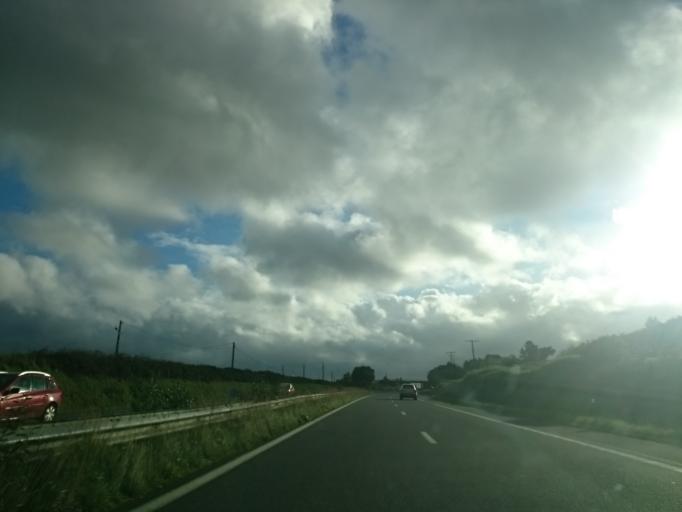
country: FR
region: Brittany
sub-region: Departement du Finistere
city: Morlaix
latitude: 48.5578
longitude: -3.8712
